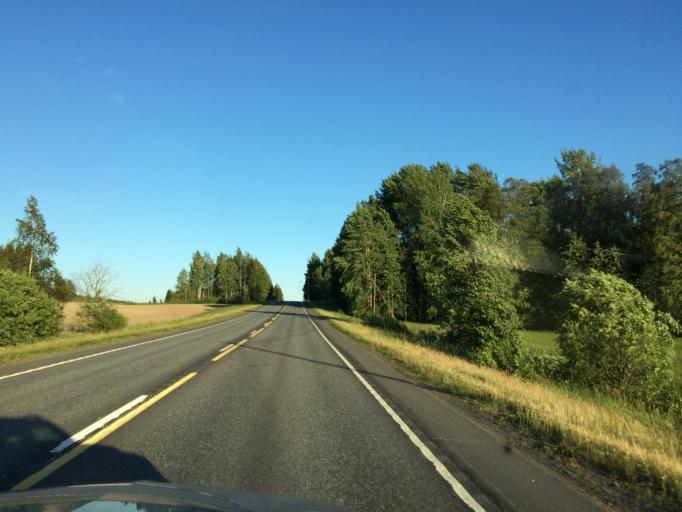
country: FI
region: Haeme
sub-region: Haemeenlinna
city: Tervakoski
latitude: 60.7933
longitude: 24.6717
